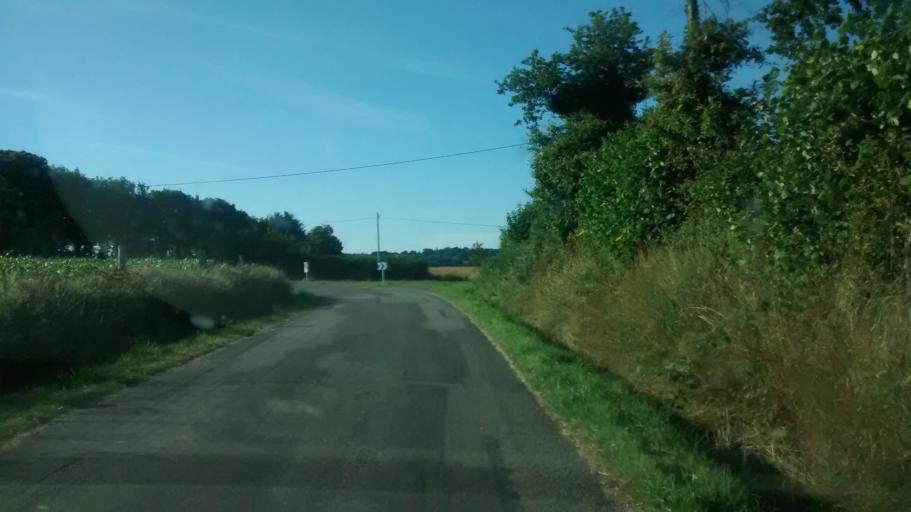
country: FR
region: Brittany
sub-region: Departement du Morbihan
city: Molac
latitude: 47.7188
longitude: -2.4600
